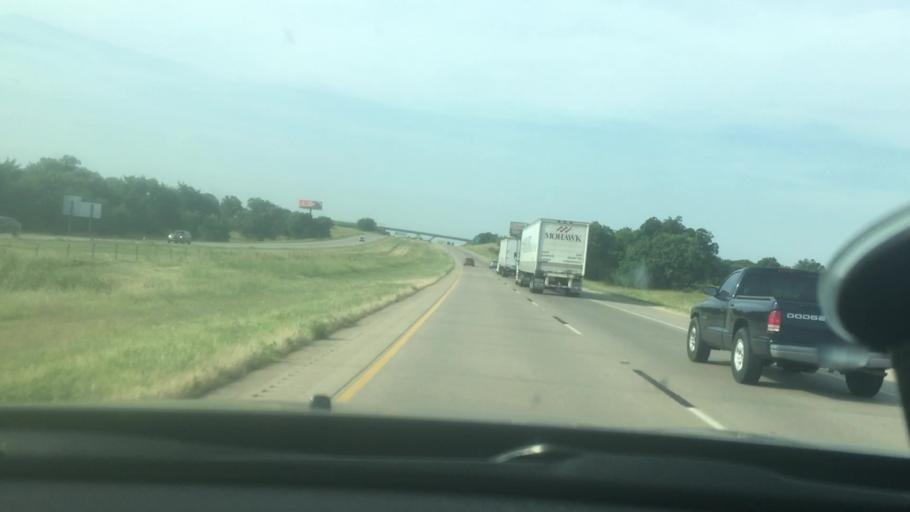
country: US
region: Oklahoma
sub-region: Carter County
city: Ardmore
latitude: 34.3251
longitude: -97.1553
